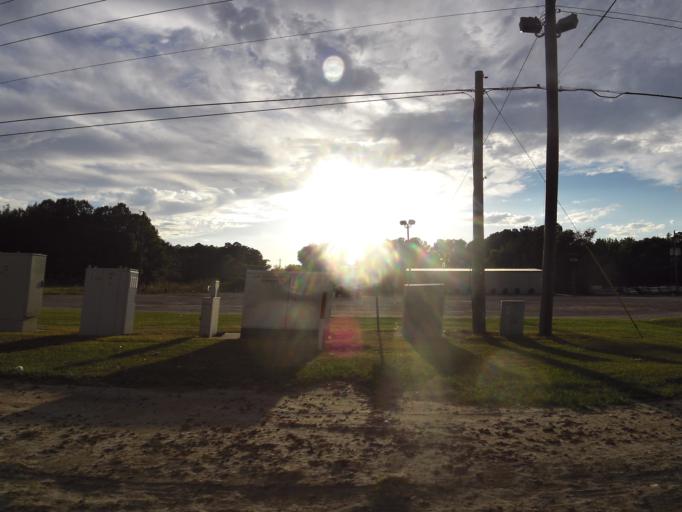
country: US
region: Georgia
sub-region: Chatham County
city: Garden City
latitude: 32.0784
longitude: -81.1960
